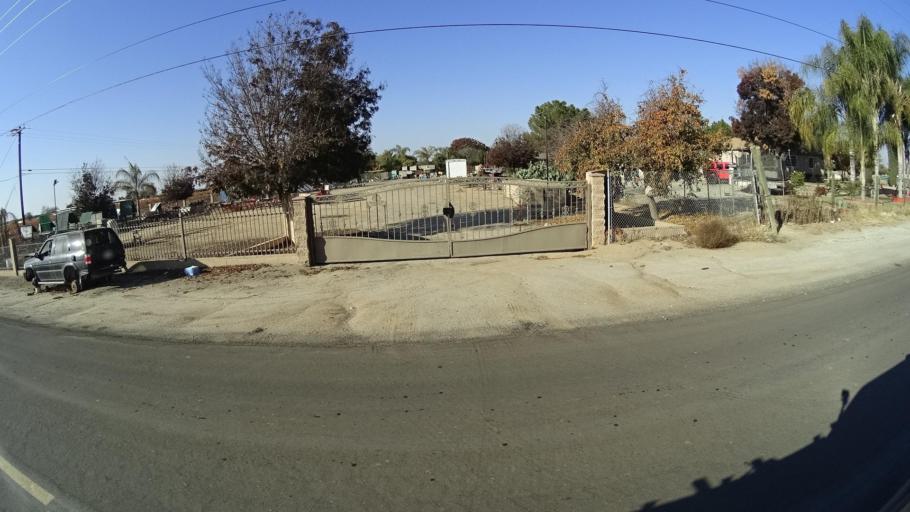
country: US
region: California
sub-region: Tulare County
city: Richgrove
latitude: 35.7473
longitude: -119.1342
